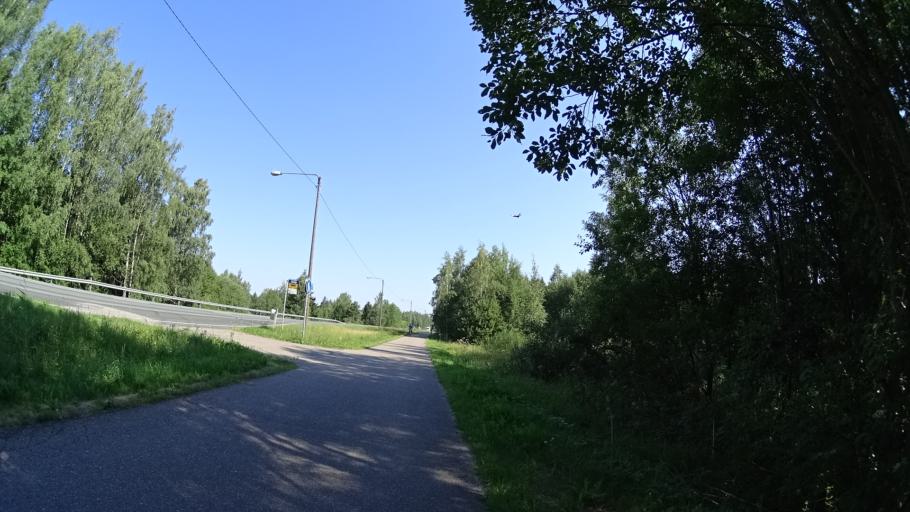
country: FI
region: Uusimaa
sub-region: Helsinki
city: Kerava
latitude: 60.3368
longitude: 25.1250
